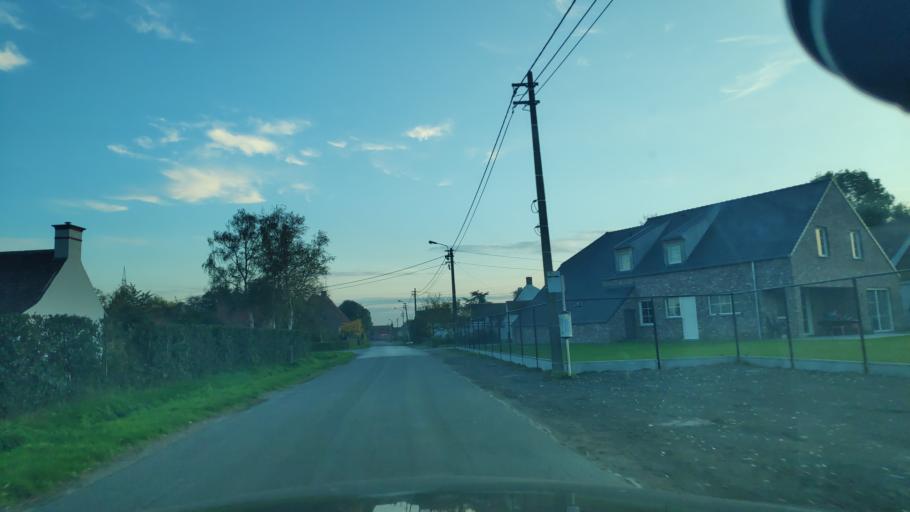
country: BE
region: Flanders
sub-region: Provincie Oost-Vlaanderen
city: Zomergem
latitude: 51.1182
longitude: 3.5045
